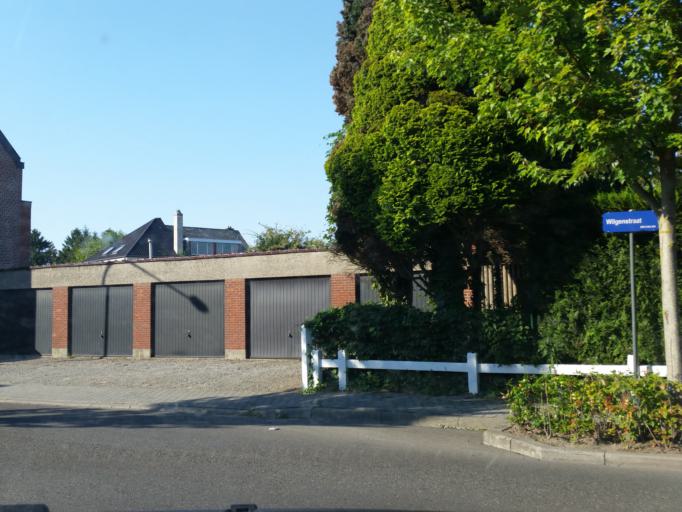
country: BE
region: Flanders
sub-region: Provincie Antwerpen
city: Mechelen
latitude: 51.0070
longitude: 4.4785
